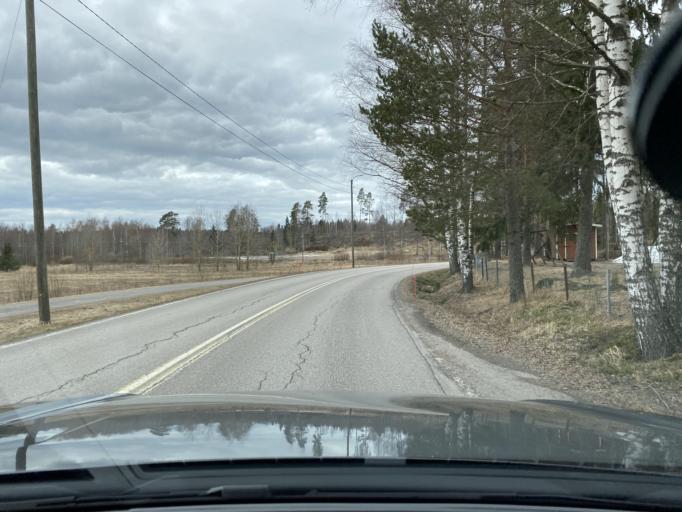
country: FI
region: Uusimaa
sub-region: Helsinki
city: Hyvinge
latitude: 60.5667
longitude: 24.8038
